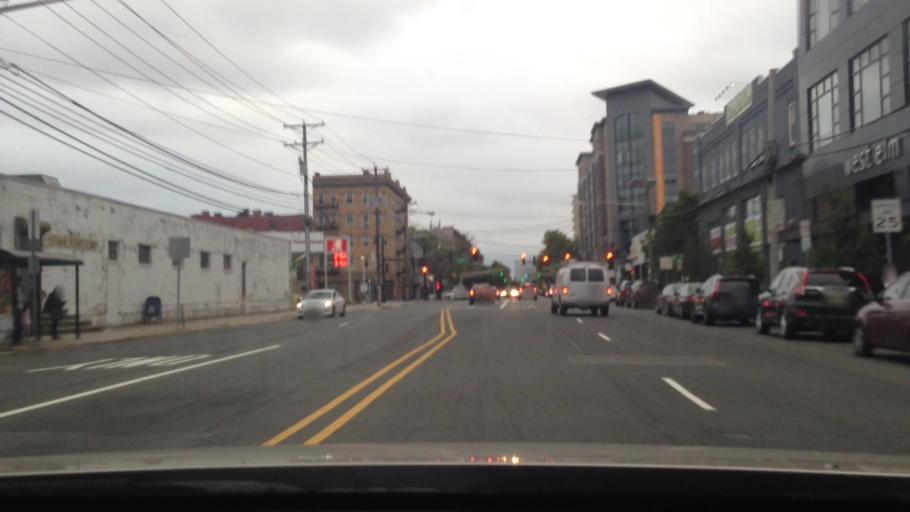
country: US
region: New Jersey
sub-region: Hudson County
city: Hoboken
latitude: 40.7550
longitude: -74.0293
